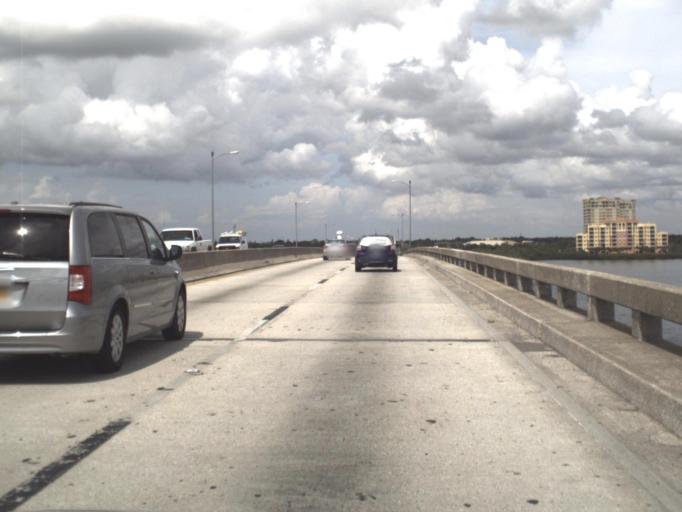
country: US
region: Florida
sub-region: Manatee County
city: Bradenton
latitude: 27.5031
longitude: -82.5630
